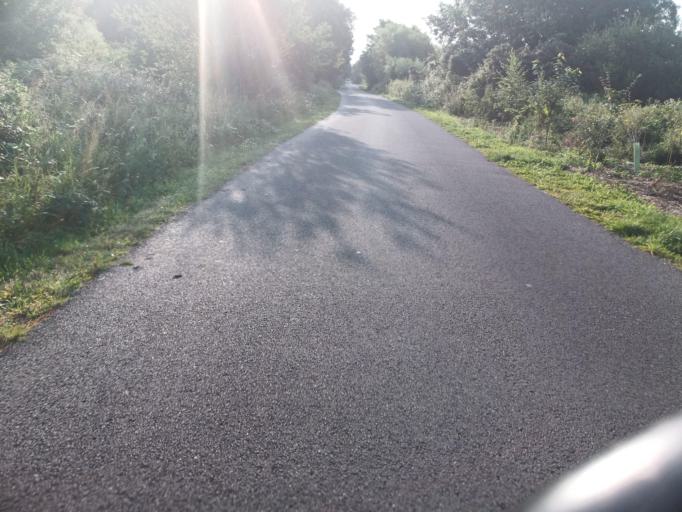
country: GB
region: Northern Ireland
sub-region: Castlereagh District
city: Dundonald
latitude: 54.5903
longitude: -5.8237
